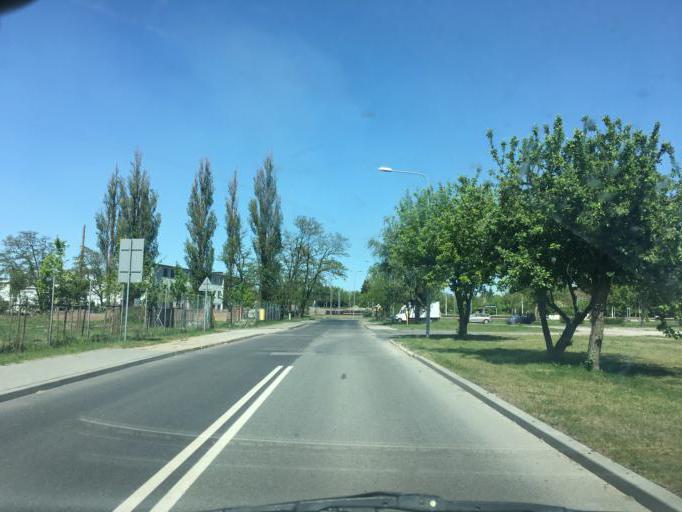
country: PL
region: Kujawsko-Pomorskie
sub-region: Powiat bydgoski
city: Osielsko
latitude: 53.1265
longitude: 18.0789
